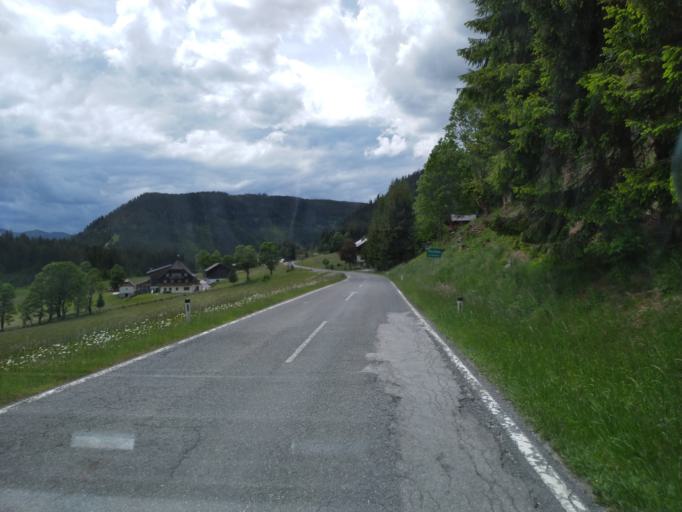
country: AT
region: Salzburg
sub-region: Politischer Bezirk Sankt Johann im Pongau
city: Filzmoos
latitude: 47.4339
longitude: 13.5686
